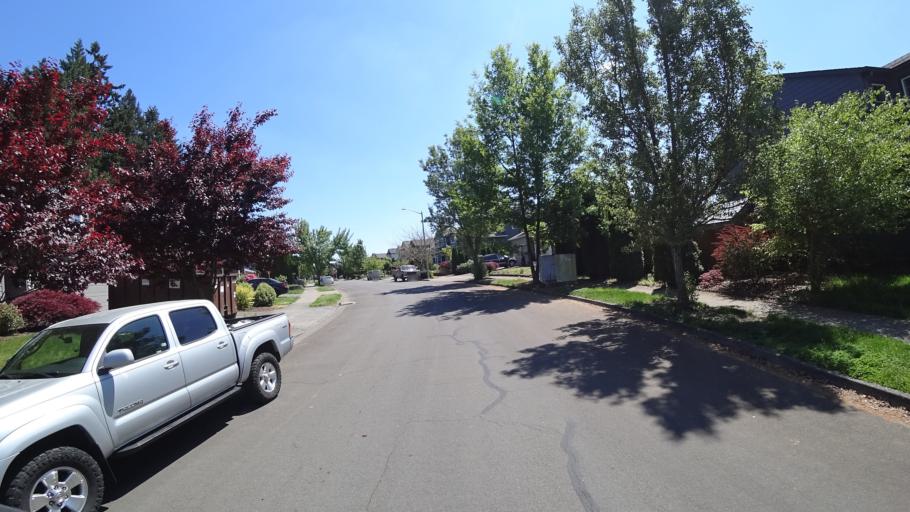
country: US
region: Oregon
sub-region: Washington County
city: Rockcreek
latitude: 45.5200
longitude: -122.9044
